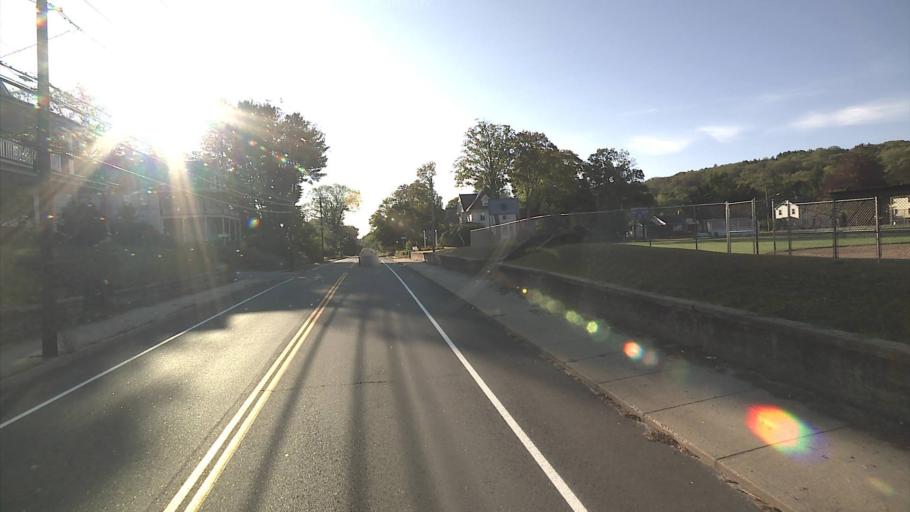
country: US
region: Connecticut
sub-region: Windham County
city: Willimantic
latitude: 41.7072
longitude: -72.2015
